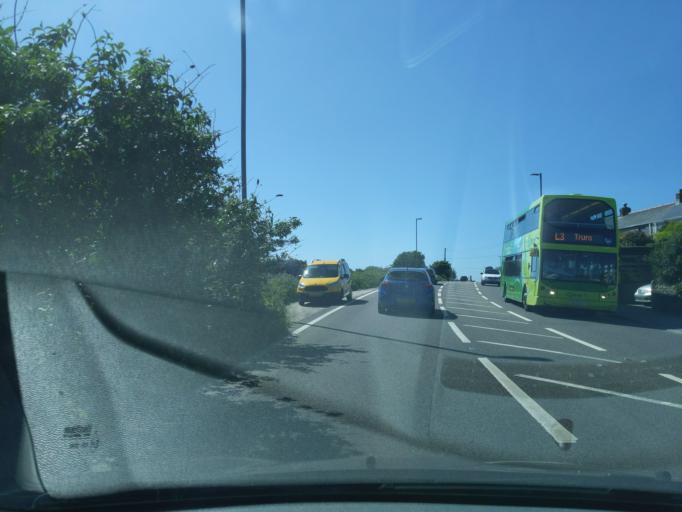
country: GB
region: England
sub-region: Cornwall
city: Penryn
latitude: 50.1643
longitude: -5.1607
